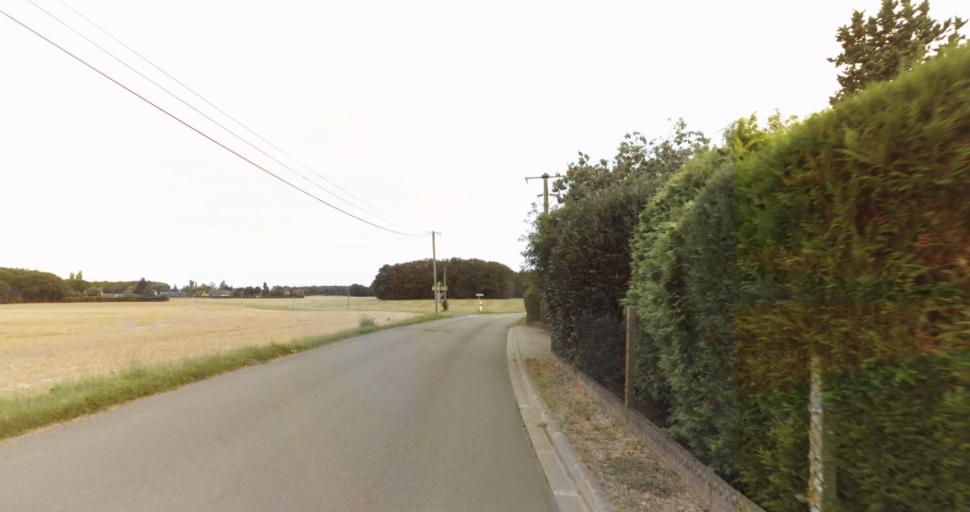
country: FR
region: Haute-Normandie
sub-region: Departement de l'Eure
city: Gravigny
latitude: 48.9853
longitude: 1.2578
